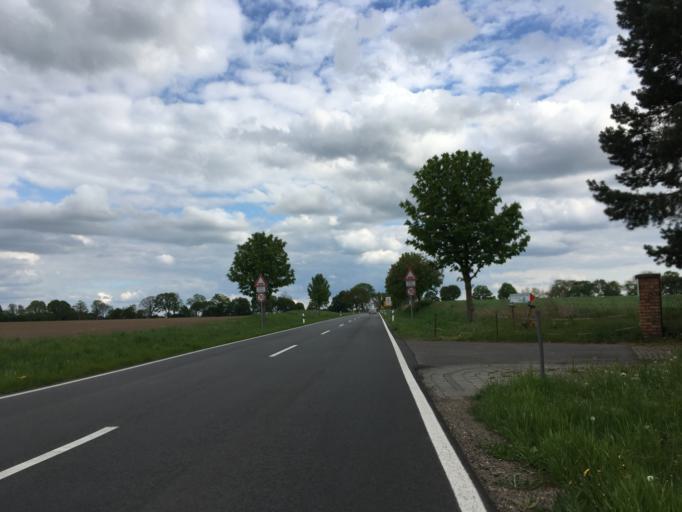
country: DE
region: Brandenburg
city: Bernau bei Berlin
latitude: 52.6575
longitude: 13.6001
